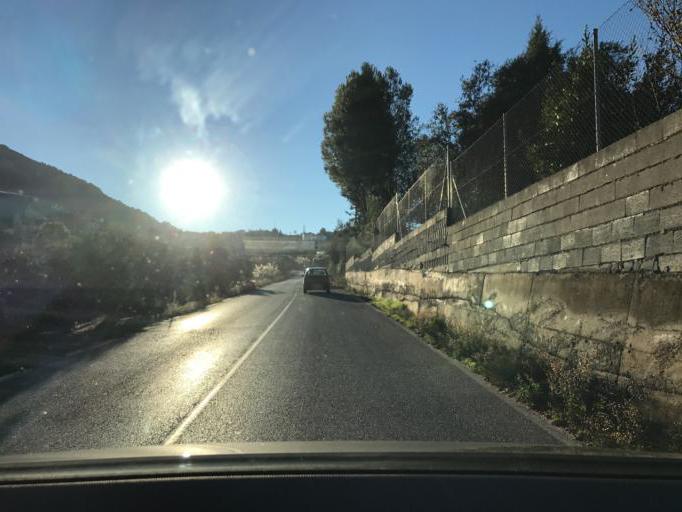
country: ES
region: Andalusia
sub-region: Provincia de Granada
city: Nivar
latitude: 37.2647
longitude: -3.5801
